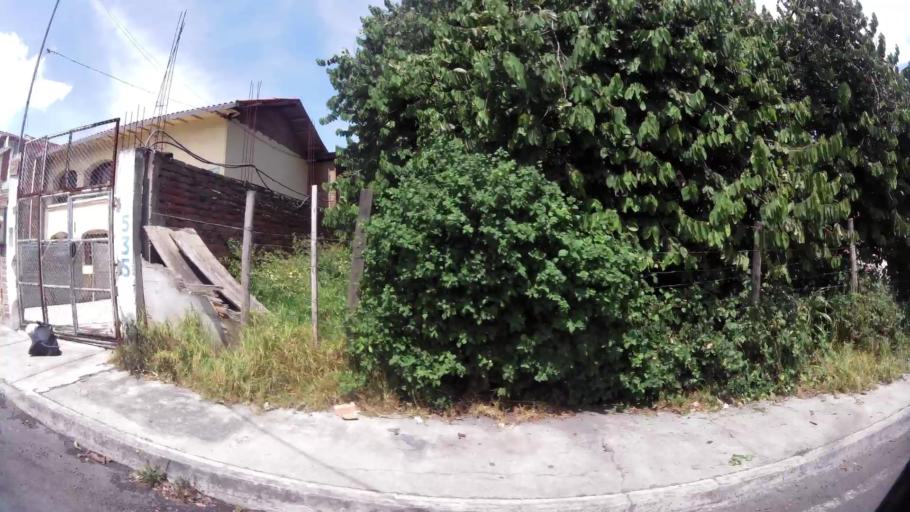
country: EC
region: Pichincha
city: Quito
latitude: -0.2133
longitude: -78.3961
